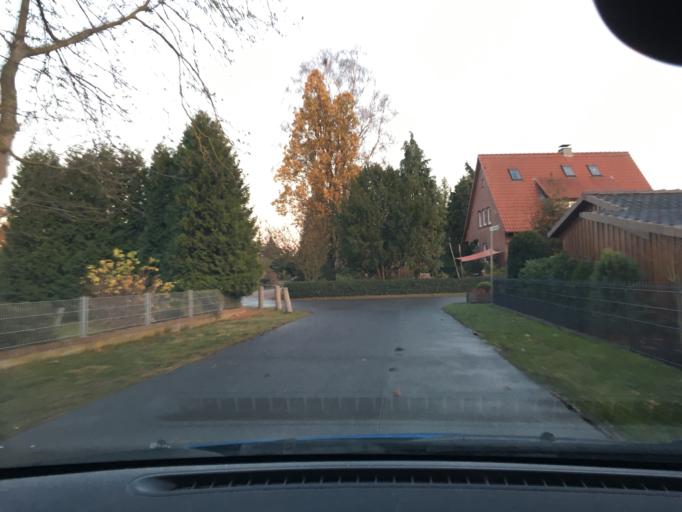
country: DE
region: Lower Saxony
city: Radbruch
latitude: 53.3347
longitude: 10.3133
